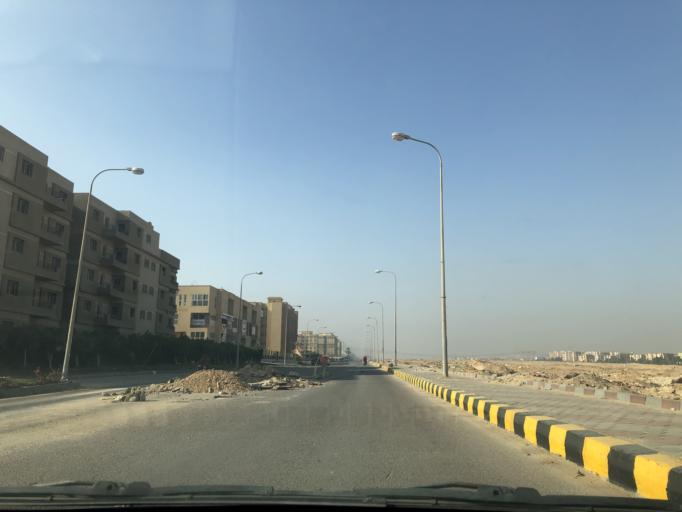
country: EG
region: Al Jizah
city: Madinat Sittah Uktubar
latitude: 29.9167
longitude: 31.0607
